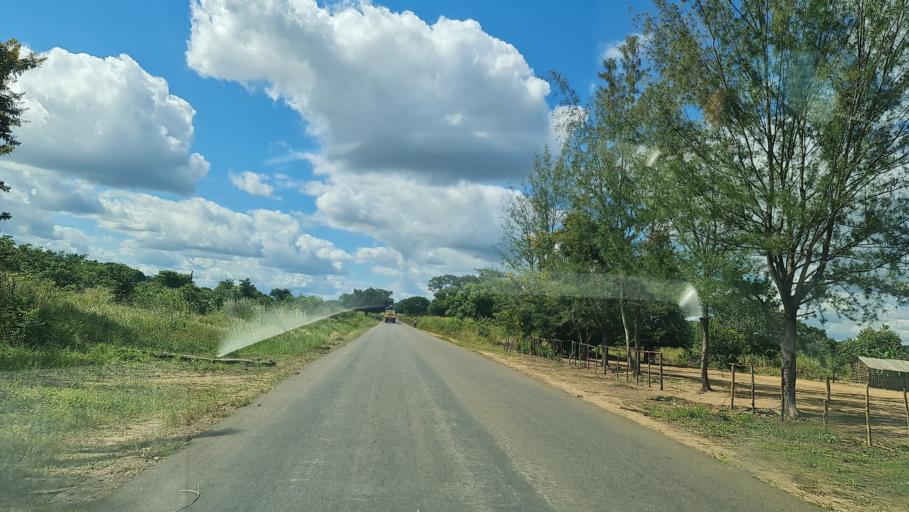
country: MZ
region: Zambezia
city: Quelimane
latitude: -17.5143
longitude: 36.2231
